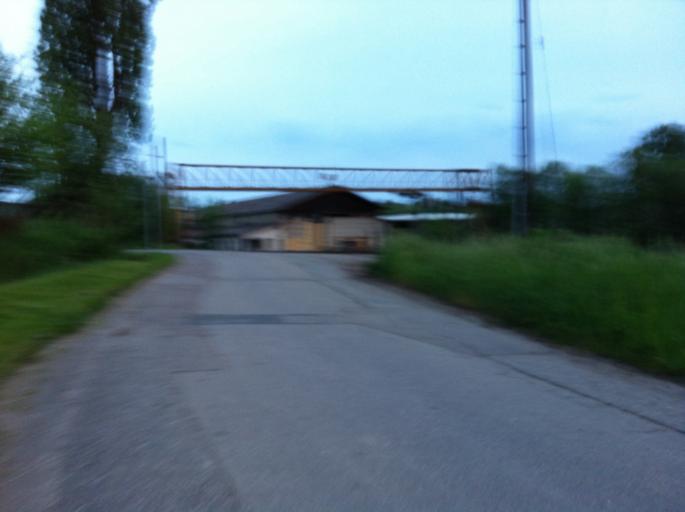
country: DE
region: Baden-Wuerttemberg
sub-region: Freiburg Region
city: Rheinfelden (Baden)
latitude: 47.5963
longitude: 7.7949
